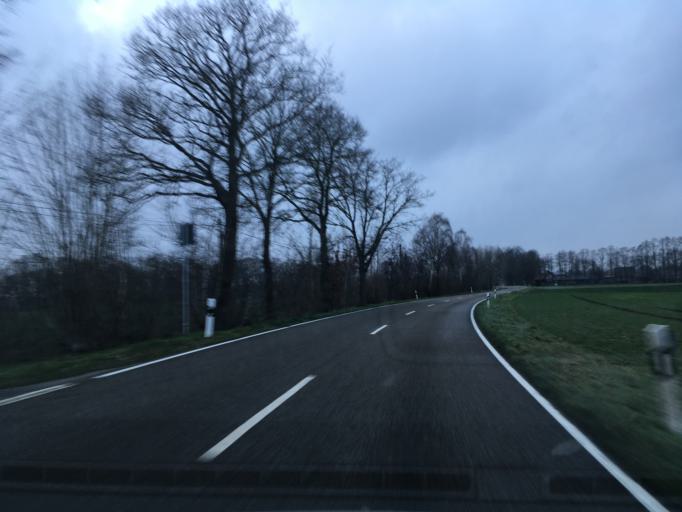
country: DE
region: North Rhine-Westphalia
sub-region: Regierungsbezirk Munster
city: Gronau
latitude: 52.1768
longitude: 7.0748
